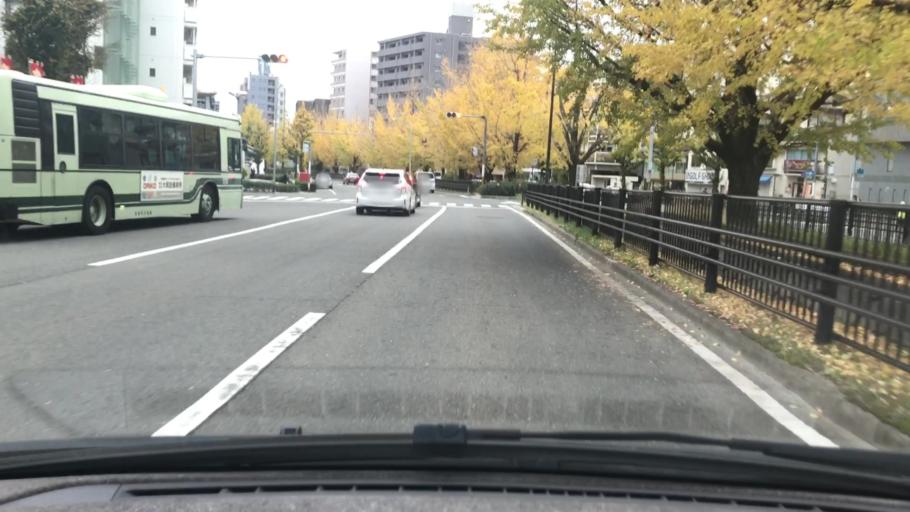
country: JP
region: Kyoto
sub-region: Kyoto-shi
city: Kamigyo-ku
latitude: 35.0363
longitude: 135.7516
